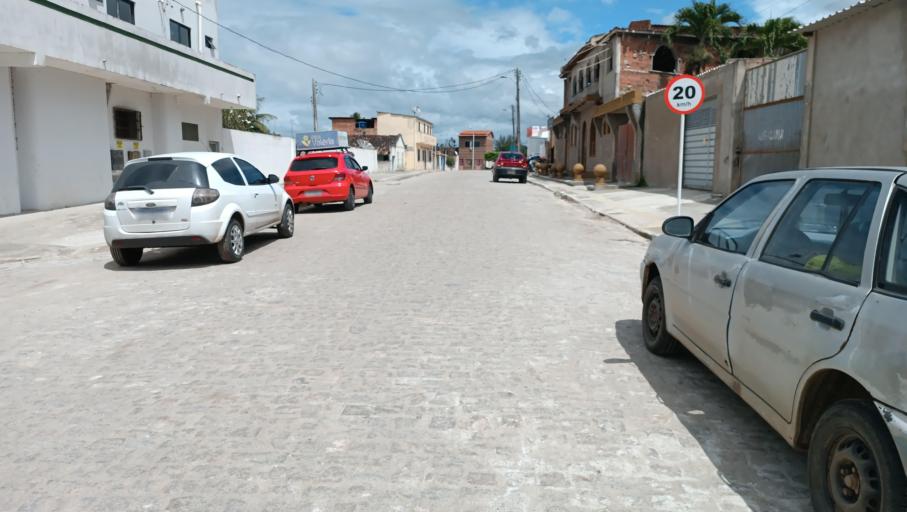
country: BR
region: Bahia
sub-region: Castro Alves
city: Castro Alves
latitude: -12.7645
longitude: -39.4240
